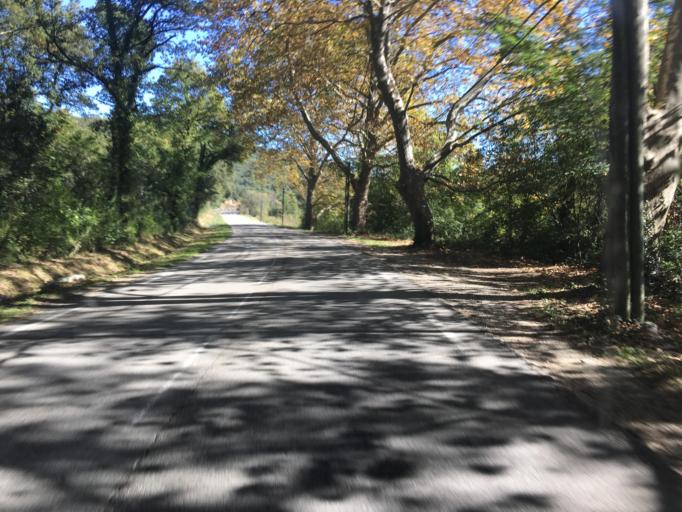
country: FR
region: Languedoc-Roussillon
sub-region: Departement du Gard
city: Quissac
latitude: 43.9200
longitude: 4.0239
